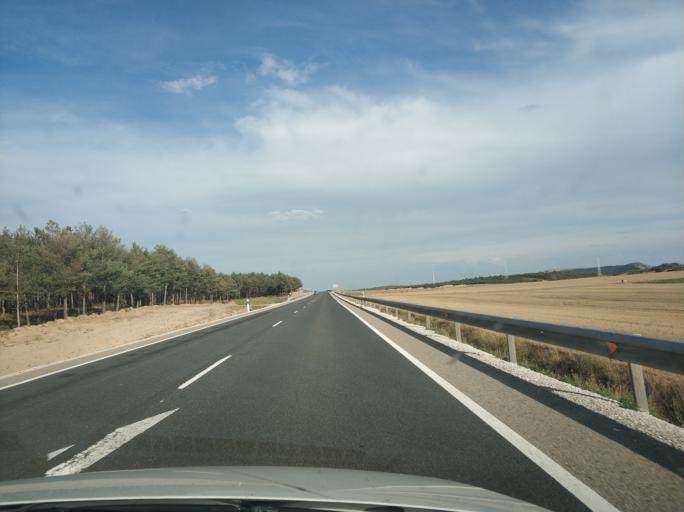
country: ES
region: Castille and Leon
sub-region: Provincia de Palencia
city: Pomar de Valdivia
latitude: 42.7352
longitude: -4.1196
